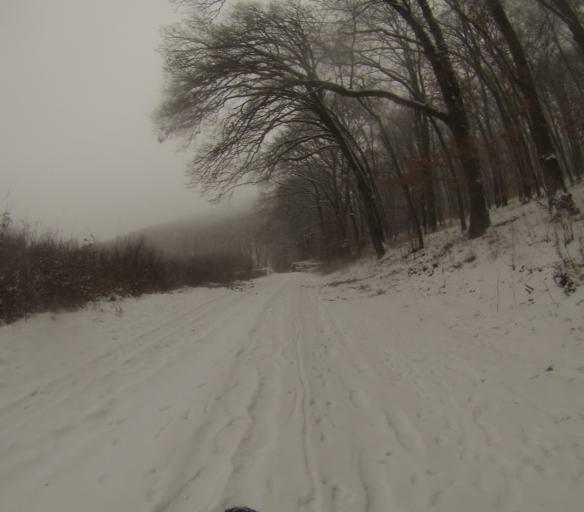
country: CZ
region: South Moravian
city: Strelice
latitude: 49.1364
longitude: 16.5195
